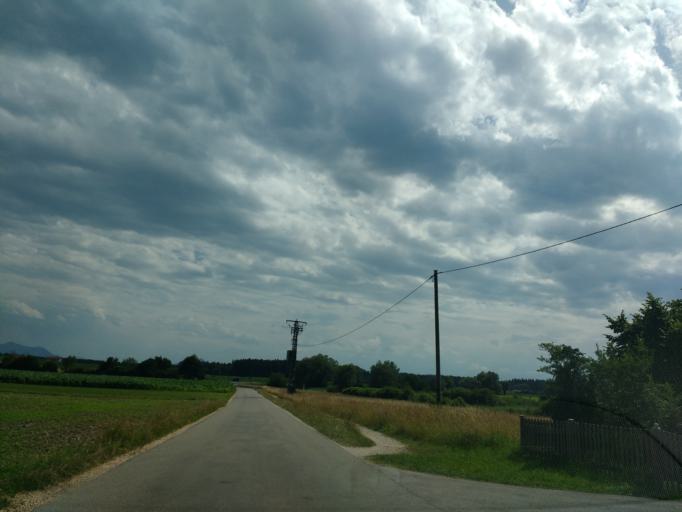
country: DE
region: Bavaria
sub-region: Upper Bavaria
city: Obing
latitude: 48.0043
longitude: 12.4226
